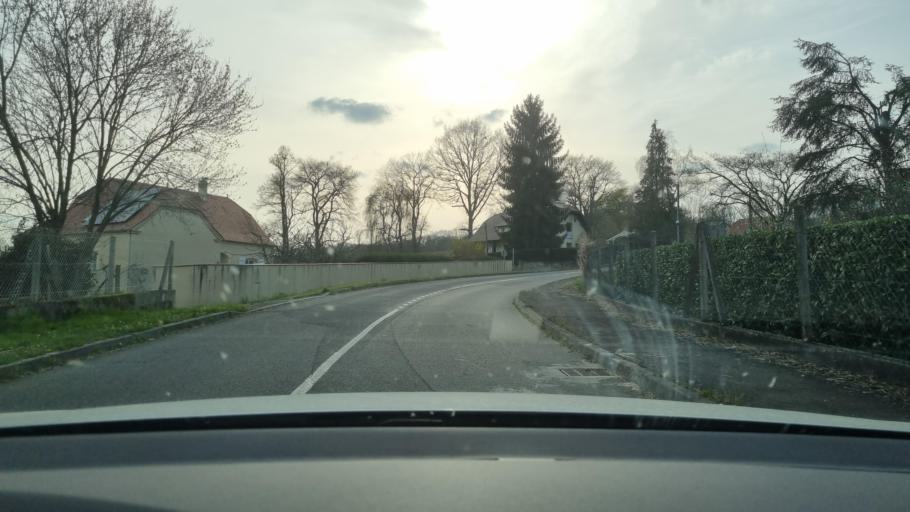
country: FR
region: Aquitaine
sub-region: Departement des Pyrenees-Atlantiques
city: Soumoulou
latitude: 43.3775
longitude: -0.1311
